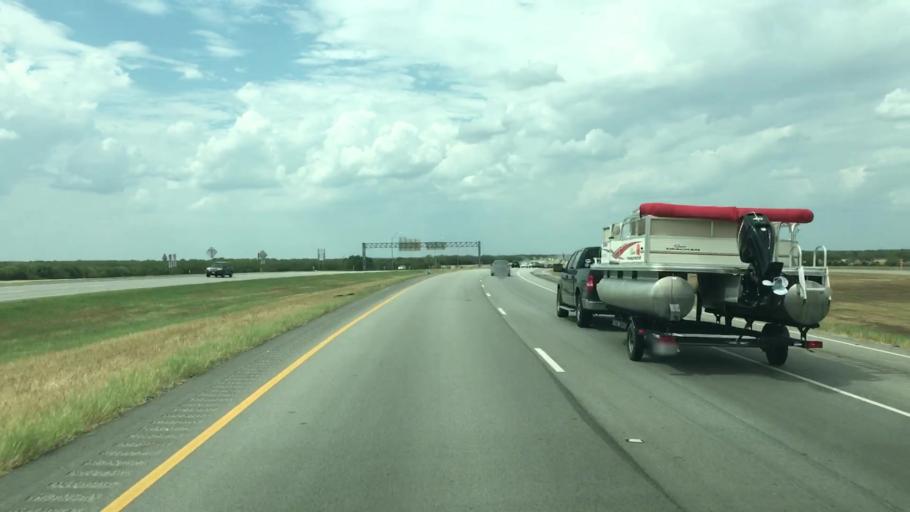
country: US
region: Texas
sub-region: Live Oak County
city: Three Rivers
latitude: 28.5266
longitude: -98.1865
